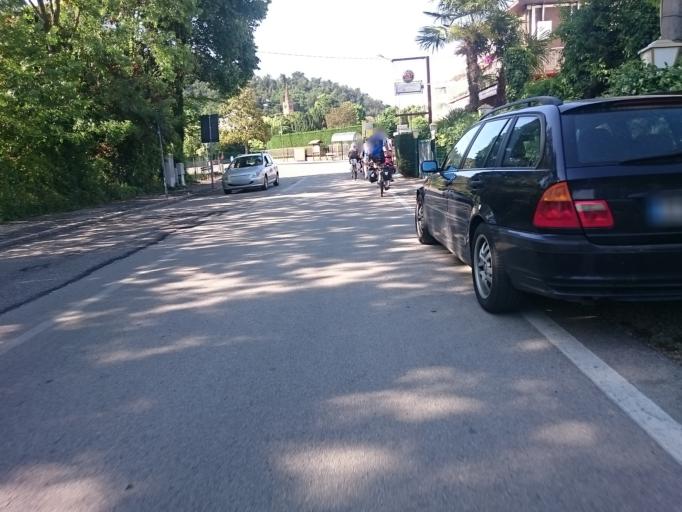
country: IT
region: Veneto
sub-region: Provincia di Padova
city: Torreglia
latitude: 45.3495
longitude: 11.7585
